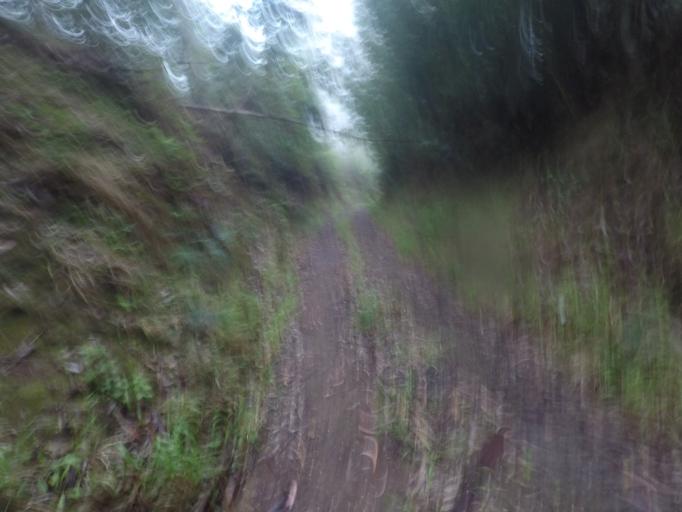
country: PT
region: Madeira
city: Ponta do Sol
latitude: 32.7118
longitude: -17.0929
